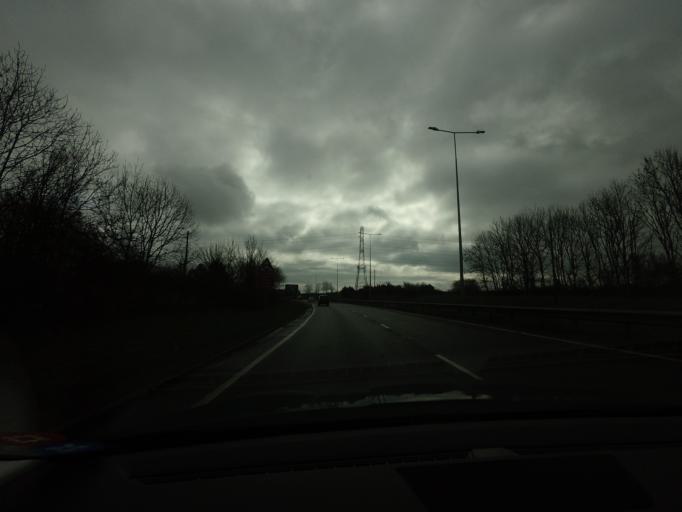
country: GB
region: England
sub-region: Kent
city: Swanley
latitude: 51.3868
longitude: 0.1954
